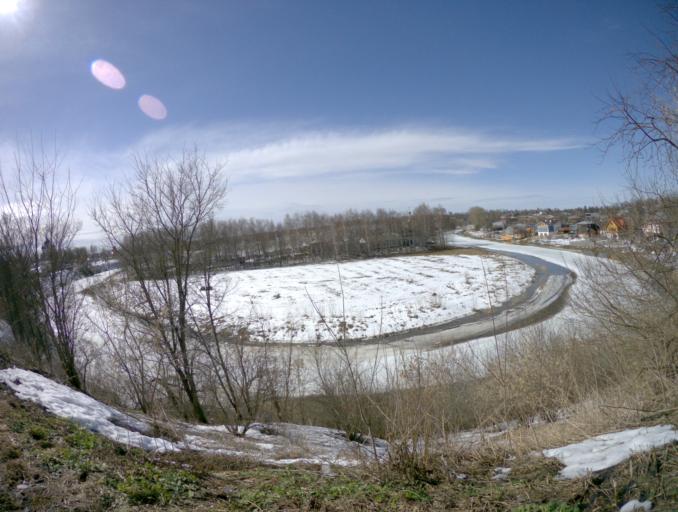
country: RU
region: Vladimir
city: Suzdal'
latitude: 56.4201
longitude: 40.4473
